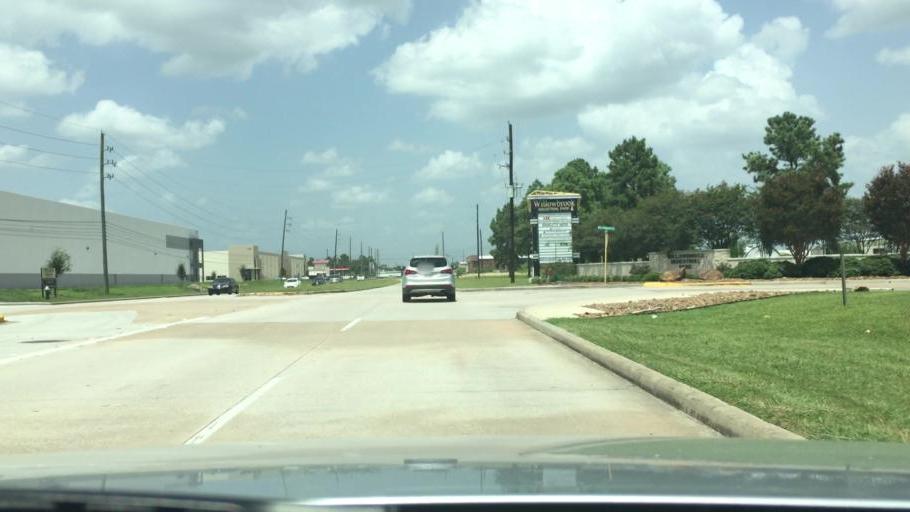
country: US
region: Texas
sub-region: Harris County
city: Hudson
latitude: 29.9523
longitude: -95.5219
